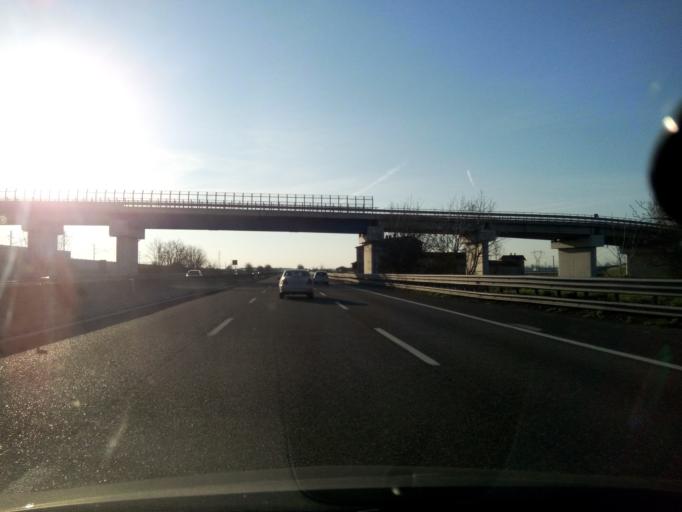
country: IT
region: Emilia-Romagna
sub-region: Provincia di Piacenza
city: Roveleto
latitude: 44.9845
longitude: 9.8541
